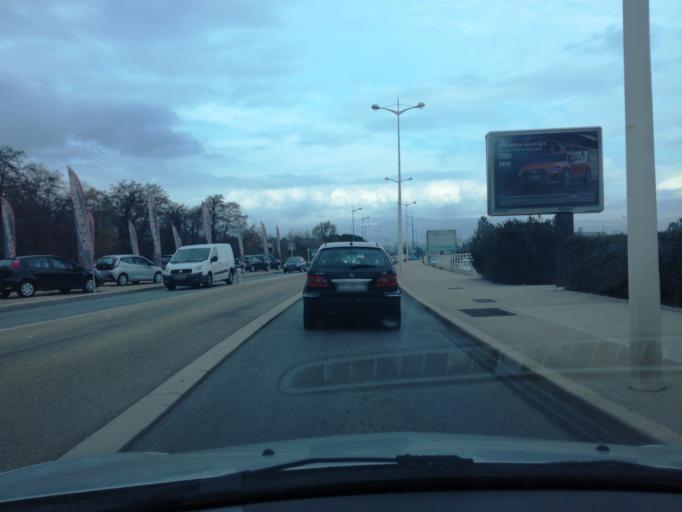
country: FR
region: Provence-Alpes-Cote d'Azur
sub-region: Departement des Alpes-Maritimes
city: Mandelieu-la-Napoule
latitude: 43.5518
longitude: 6.9556
